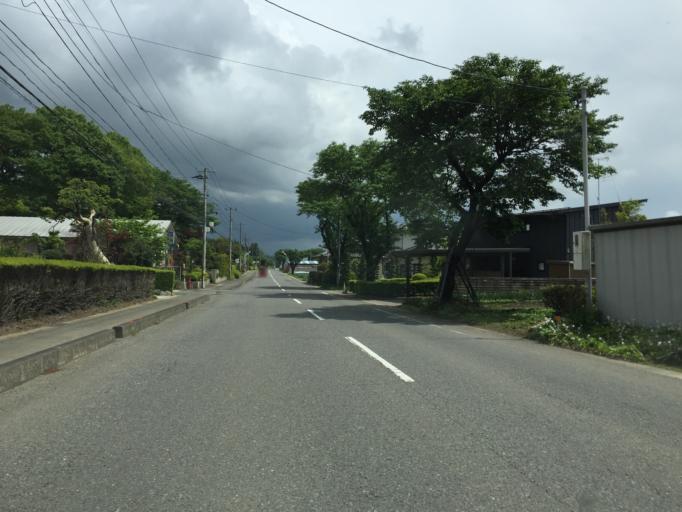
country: JP
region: Fukushima
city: Ishikawa
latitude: 37.1111
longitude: 140.3306
